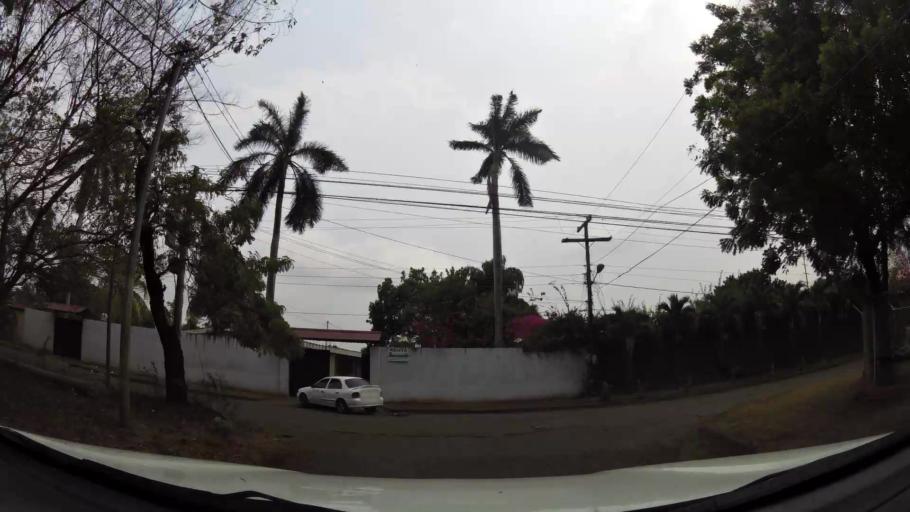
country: NI
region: Chinandega
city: Chinandega
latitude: 12.6316
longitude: -87.1177
